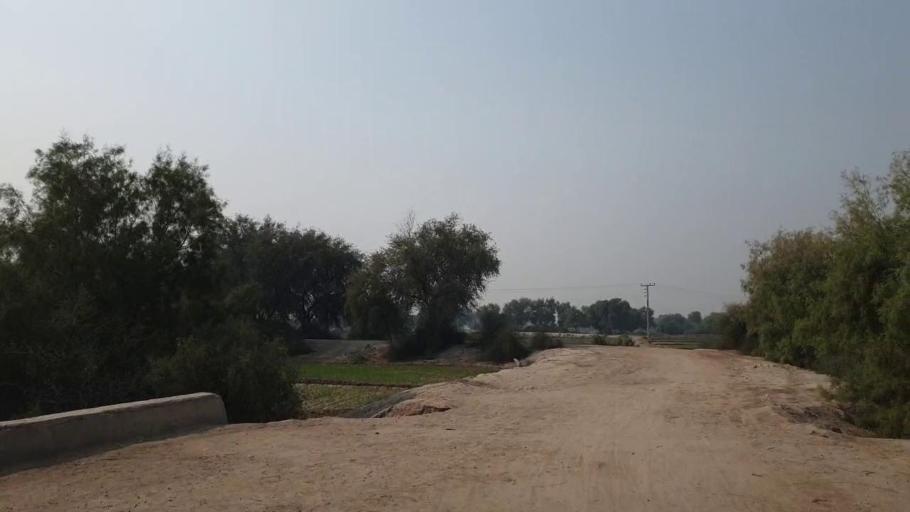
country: PK
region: Sindh
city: Bhan
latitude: 26.5147
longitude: 67.7422
